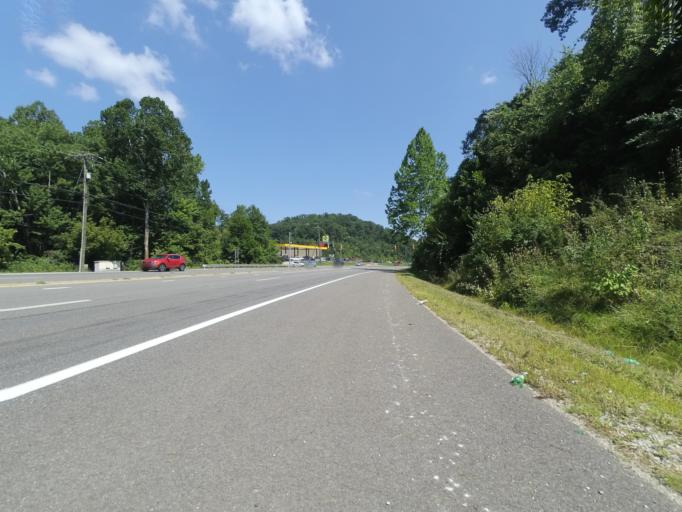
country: US
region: West Virginia
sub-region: Cabell County
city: Huntington
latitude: 38.3864
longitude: -82.4569
